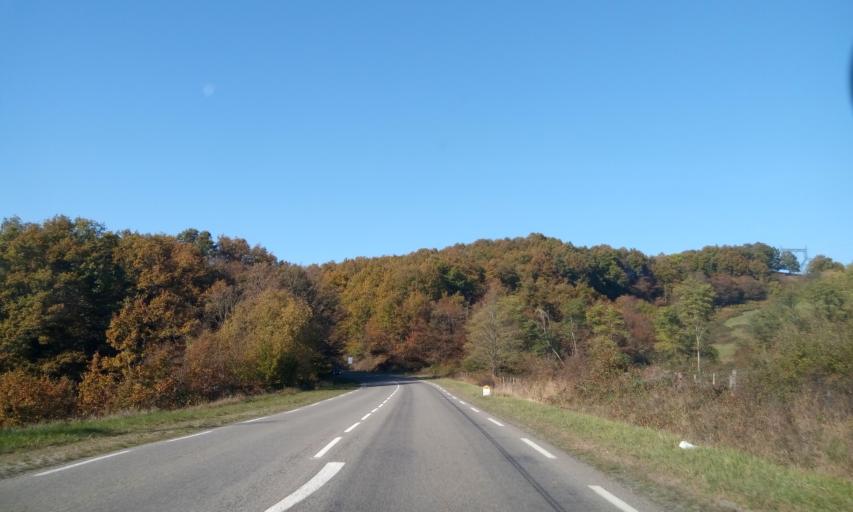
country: FR
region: Rhone-Alpes
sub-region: Departement du Rhone
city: Bourg-de-Thizy
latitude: 46.0328
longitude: 4.2590
